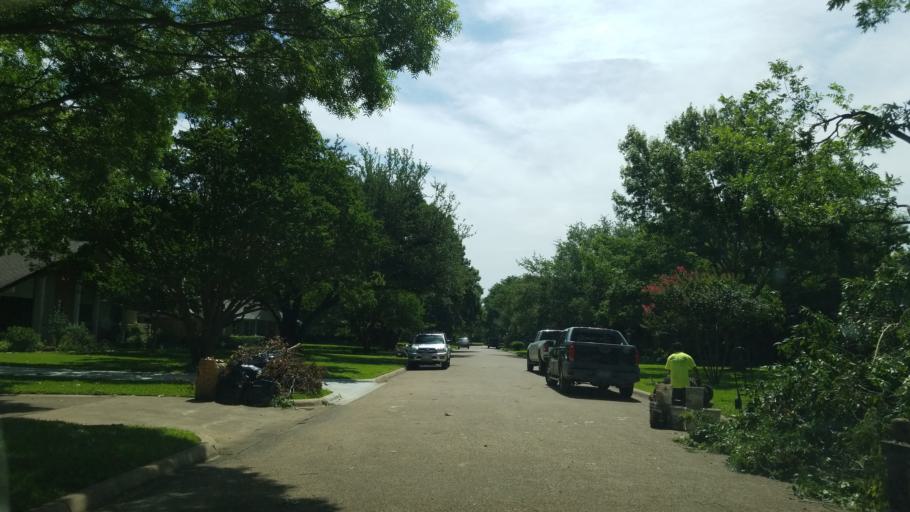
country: US
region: Texas
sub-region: Dallas County
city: Farmers Branch
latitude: 32.9061
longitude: -96.8498
